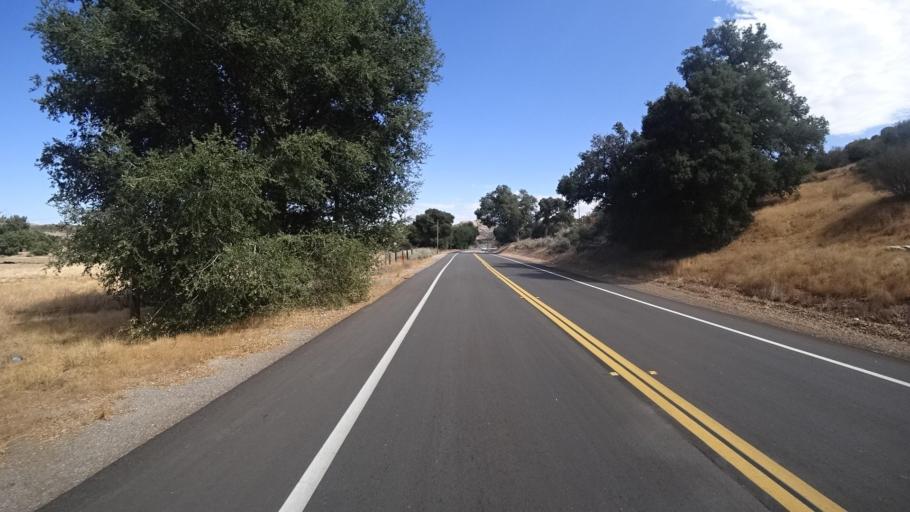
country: MX
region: Baja California
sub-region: Tecate
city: Cereso del Hongo
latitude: 32.6644
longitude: -116.2620
